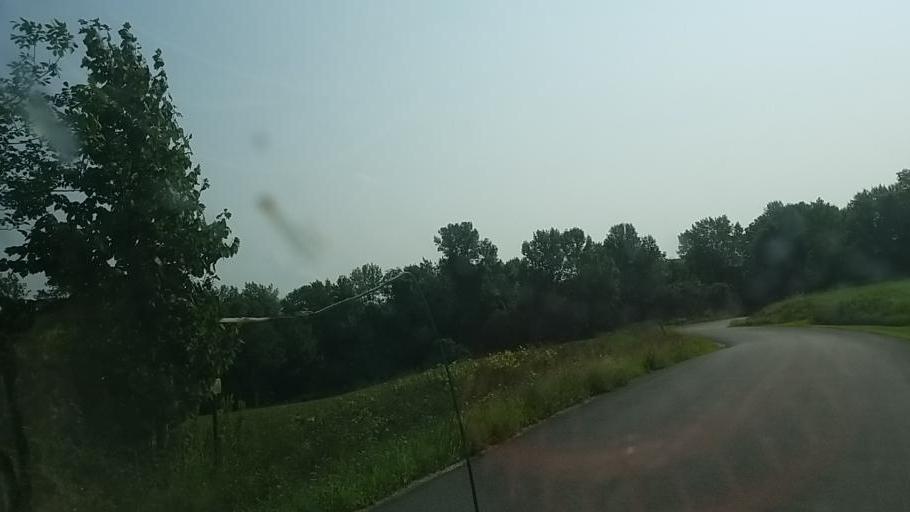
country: US
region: New York
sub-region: Montgomery County
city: Fonda
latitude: 42.9154
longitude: -74.3475
